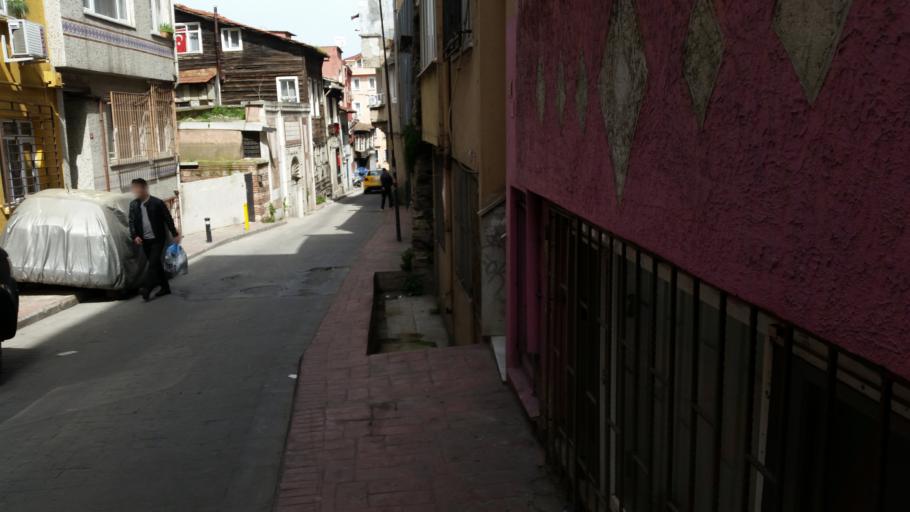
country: TR
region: Istanbul
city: Eminoenue
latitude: 41.0349
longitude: 28.9711
